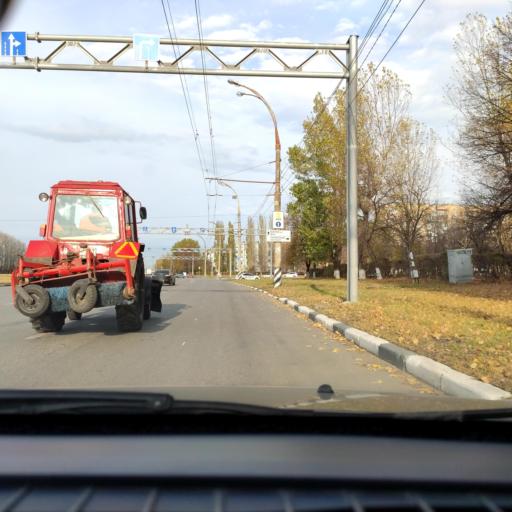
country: RU
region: Samara
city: Tol'yatti
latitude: 53.5202
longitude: 49.2596
